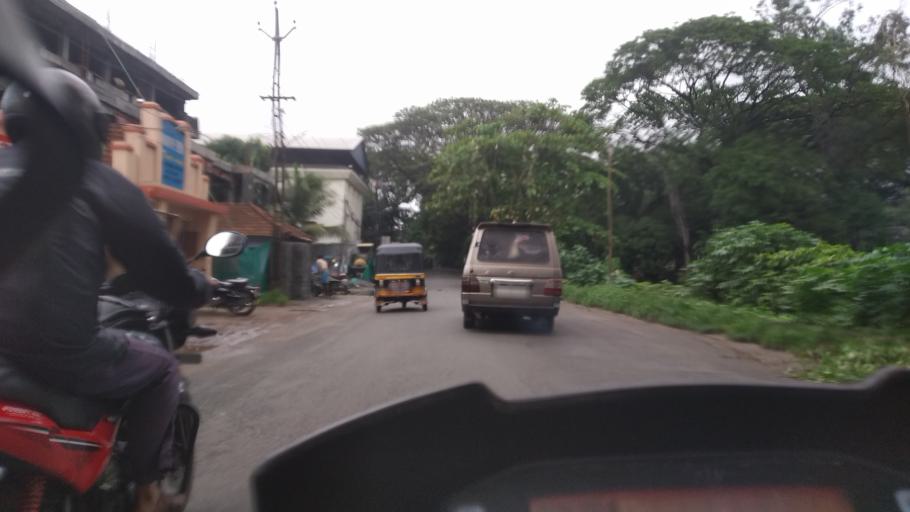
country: IN
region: Kerala
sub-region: Alappuzha
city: Alleppey
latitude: 9.5004
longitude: 76.3379
